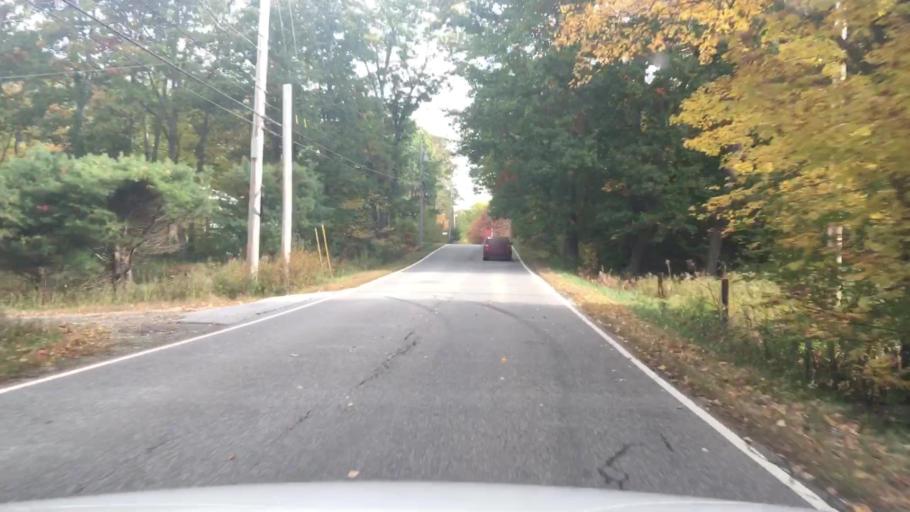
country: US
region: Maine
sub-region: Knox County
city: Rockport
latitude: 44.1744
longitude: -69.1207
